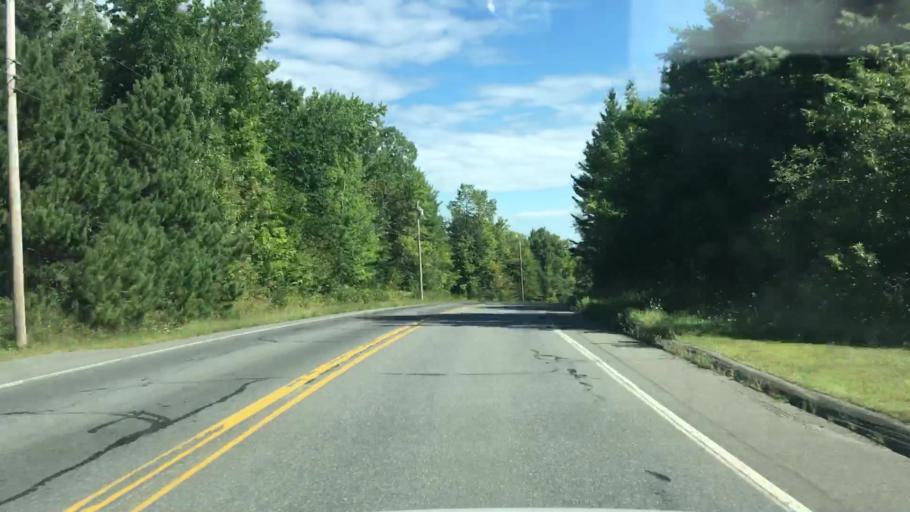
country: US
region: Maine
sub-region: Penobscot County
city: Garland
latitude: 45.0876
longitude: -69.2241
